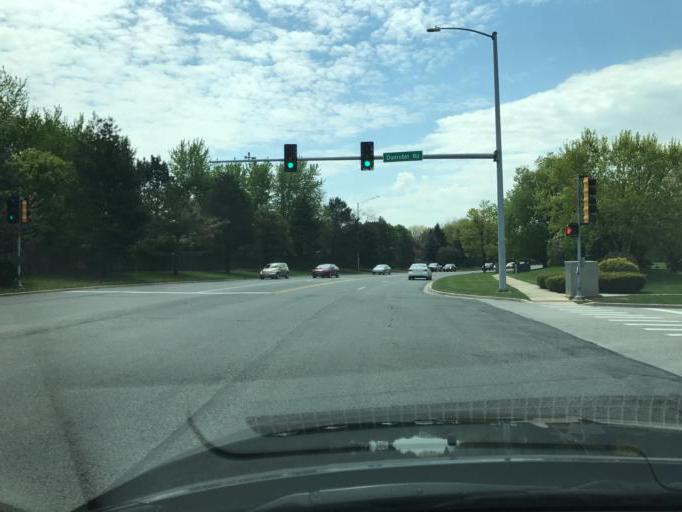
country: US
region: Illinois
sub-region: DuPage County
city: Naperville
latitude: 41.7703
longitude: -88.1108
